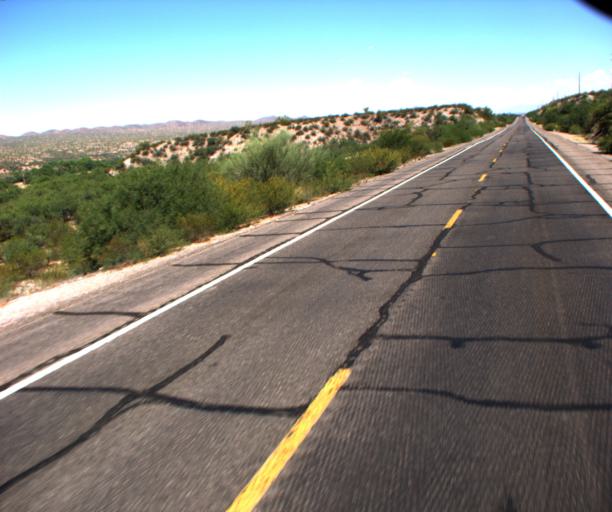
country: US
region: Arizona
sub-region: Pinal County
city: Mammoth
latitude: 32.7676
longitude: -110.6569
